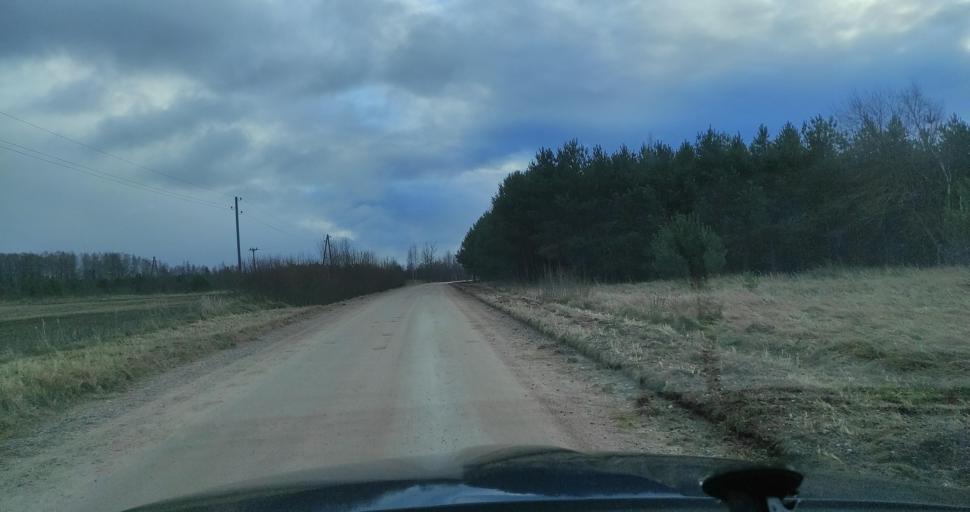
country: LV
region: Pavilostas
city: Pavilosta
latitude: 56.7731
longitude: 21.0743
